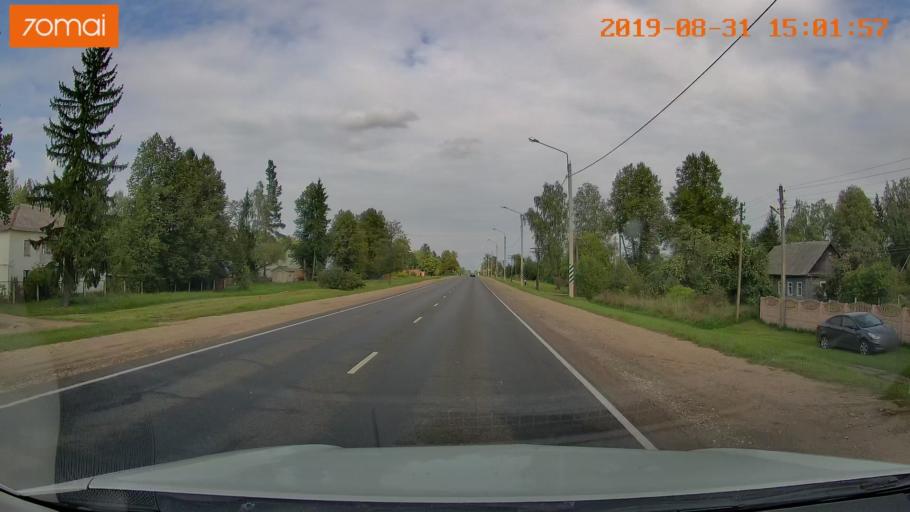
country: RU
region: Kaluga
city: Spas-Demensk
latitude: 54.3425
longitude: 34.0666
